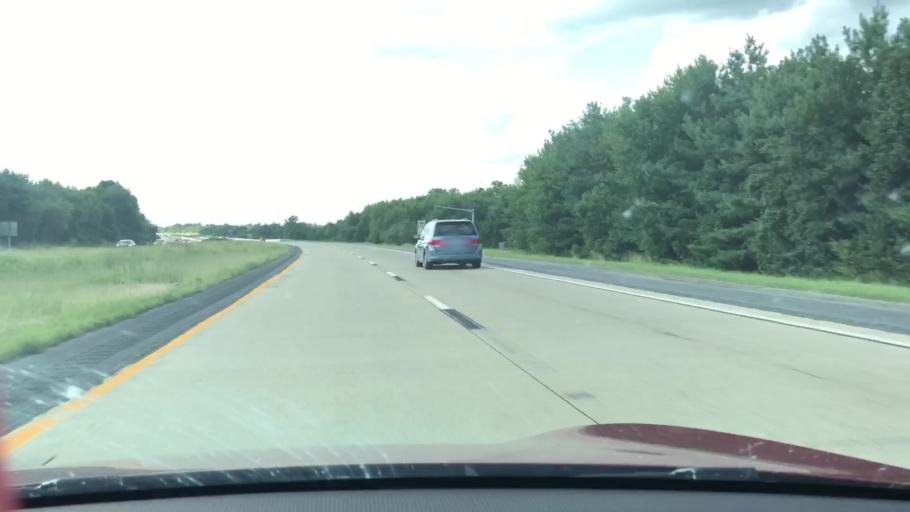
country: US
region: Delaware
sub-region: Kent County
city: Smyrna
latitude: 39.3058
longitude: -75.5941
